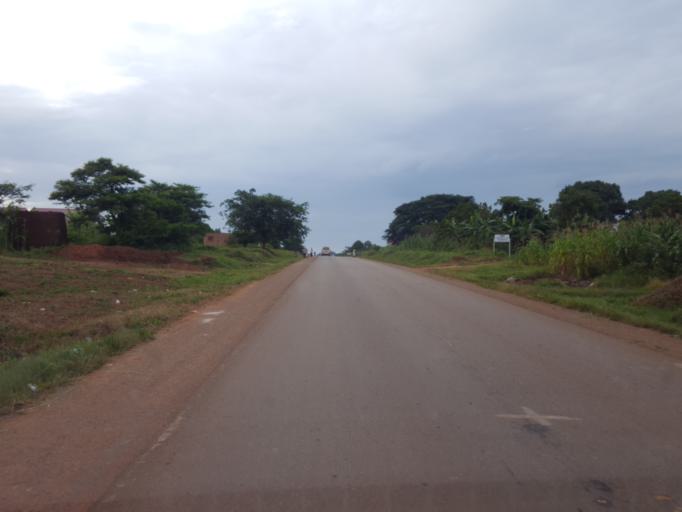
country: UG
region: Central Region
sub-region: Kyankwanzi District
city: Kyankwanzi
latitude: 1.1229
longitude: 31.5985
